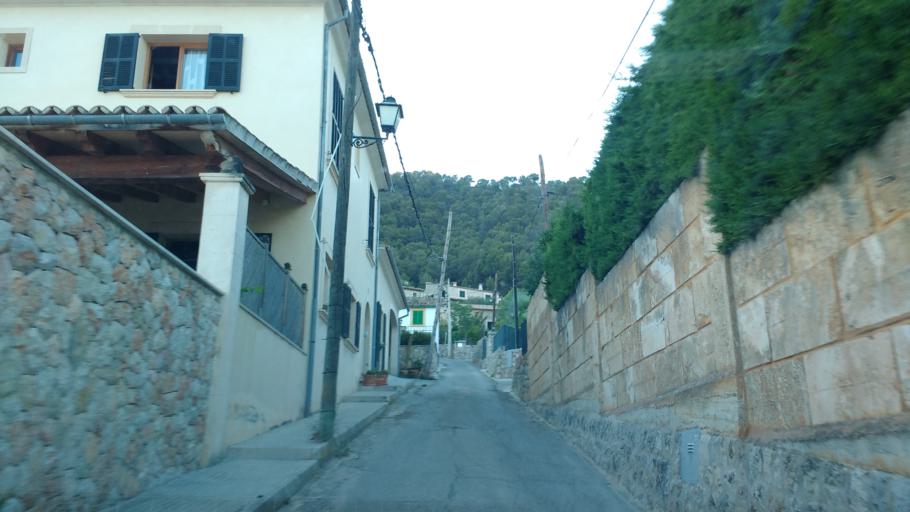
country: ES
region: Balearic Islands
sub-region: Illes Balears
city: Alaro
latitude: 39.7096
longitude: 2.7908
